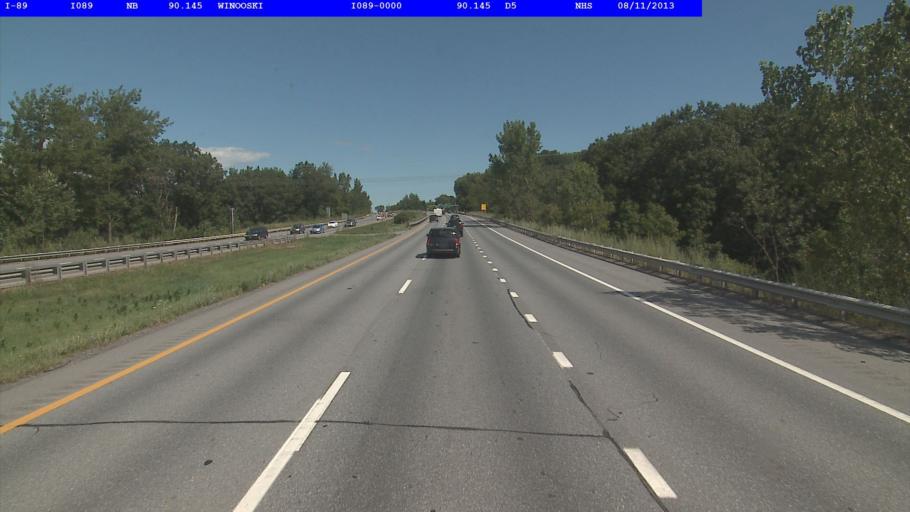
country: US
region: Vermont
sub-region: Chittenden County
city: Winooski
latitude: 44.4883
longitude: -73.1733
